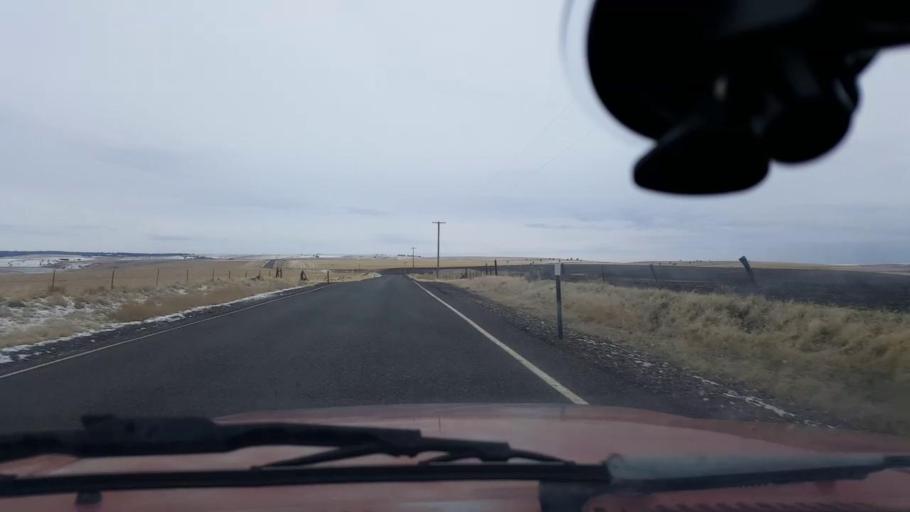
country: US
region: Washington
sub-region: Garfield County
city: Pomeroy
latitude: 46.3240
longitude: -117.3615
